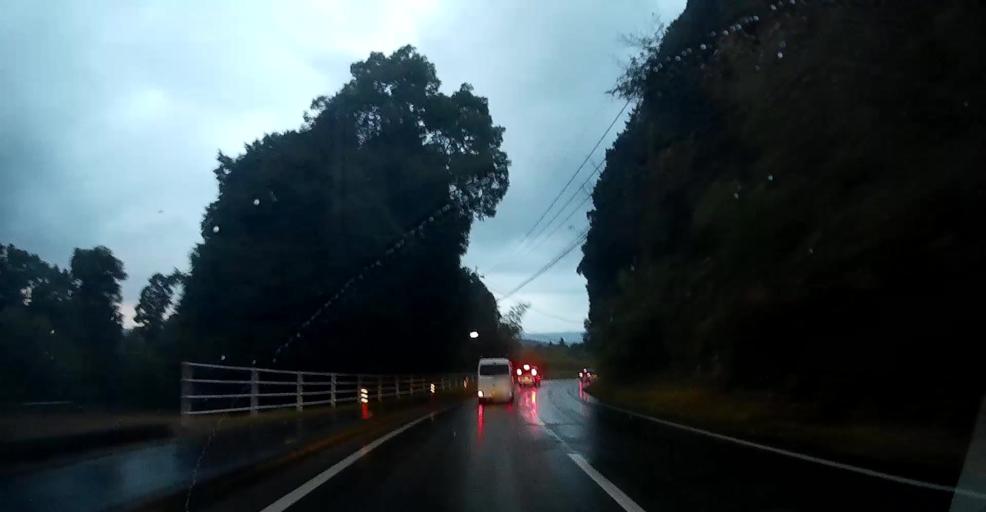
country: JP
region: Kumamoto
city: Ozu
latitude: 32.8344
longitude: 130.9150
